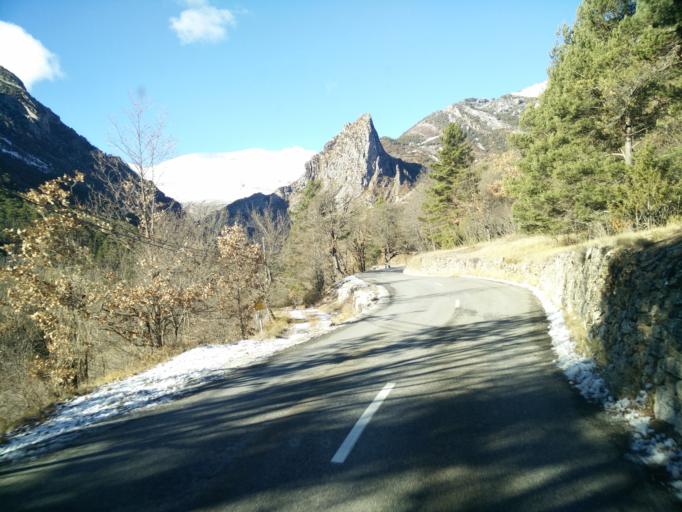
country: FR
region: Provence-Alpes-Cote d'Azur
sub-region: Departement des Alpes-de-Haute-Provence
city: Castellane
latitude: 43.8279
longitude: 6.4611
